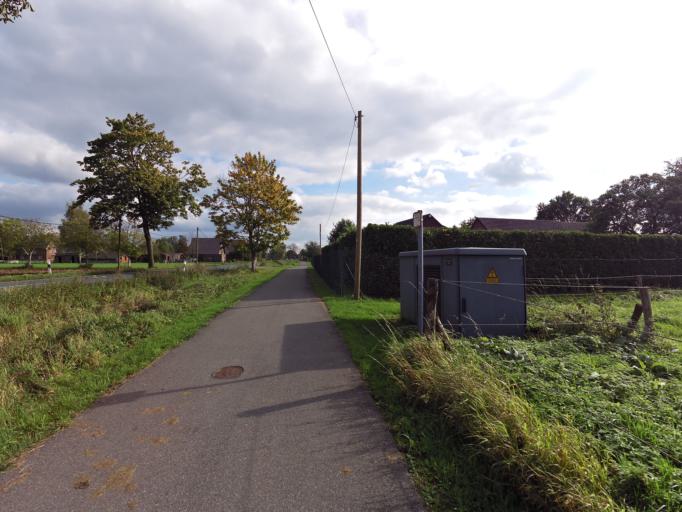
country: DE
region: North Rhine-Westphalia
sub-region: Regierungsbezirk Dusseldorf
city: Mehrhoog
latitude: 51.7836
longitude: 6.5389
